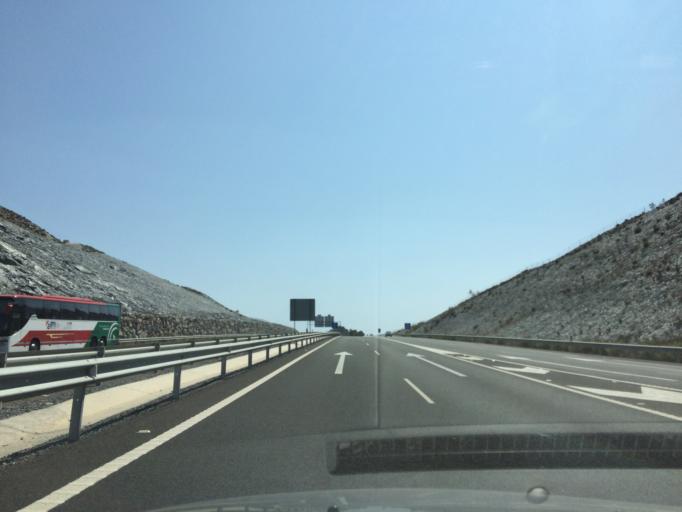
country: ES
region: Andalusia
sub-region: Provincia de Granada
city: Motril
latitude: 36.7824
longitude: -3.5055
